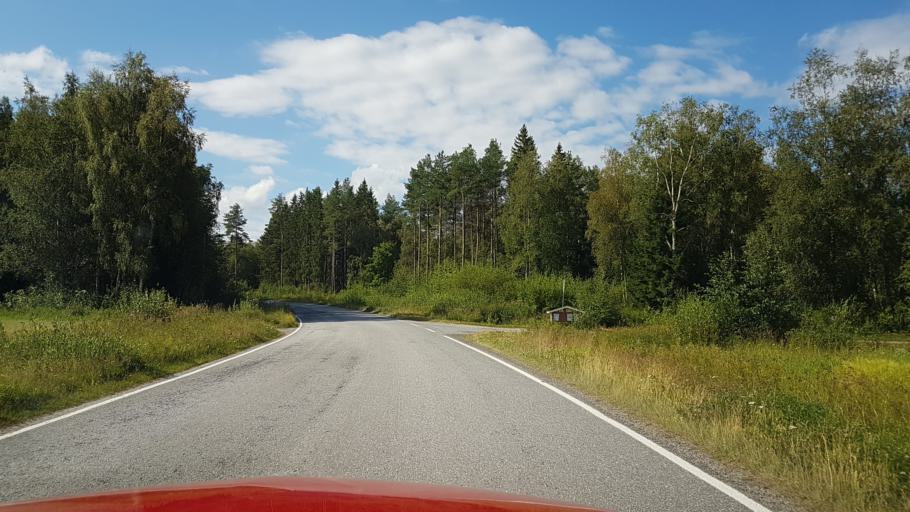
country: FI
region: Northern Ostrobothnia
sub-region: Ylivieska
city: Himanka
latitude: 64.0932
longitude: 23.7657
